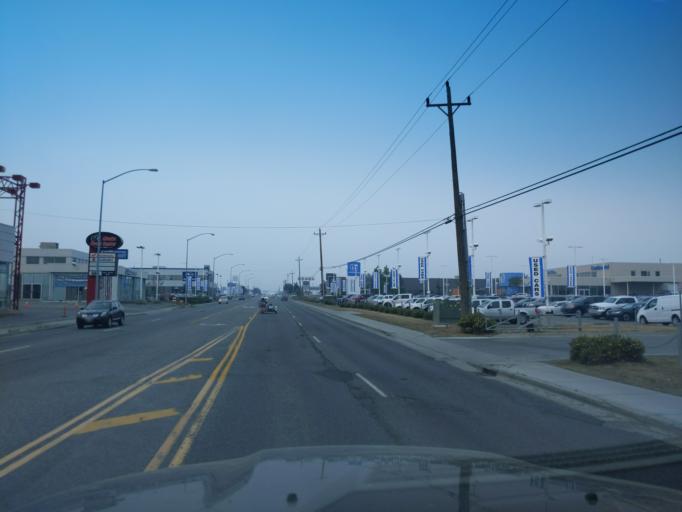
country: US
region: Alaska
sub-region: Anchorage Municipality
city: Anchorage
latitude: 61.1742
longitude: -149.8680
